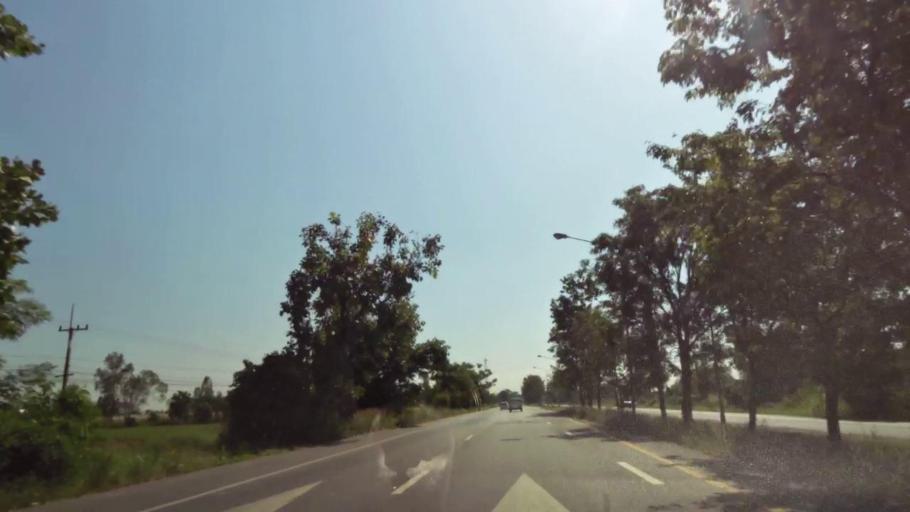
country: TH
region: Nakhon Sawan
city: Kao Liao
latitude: 15.8771
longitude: 100.1160
